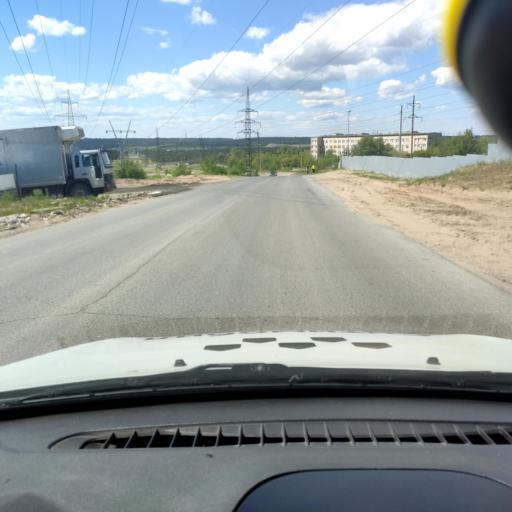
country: RU
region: Samara
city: Zhigulevsk
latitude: 53.4891
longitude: 49.5331
